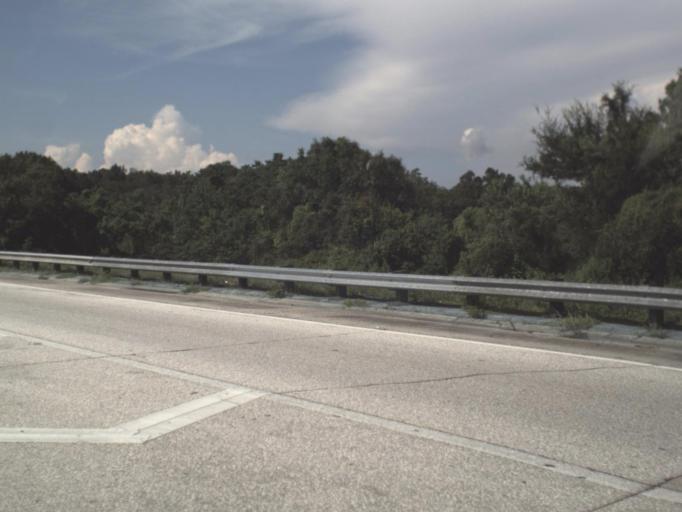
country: US
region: Florida
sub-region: Hillsborough County
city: Mango
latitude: 27.9952
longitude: -82.3267
